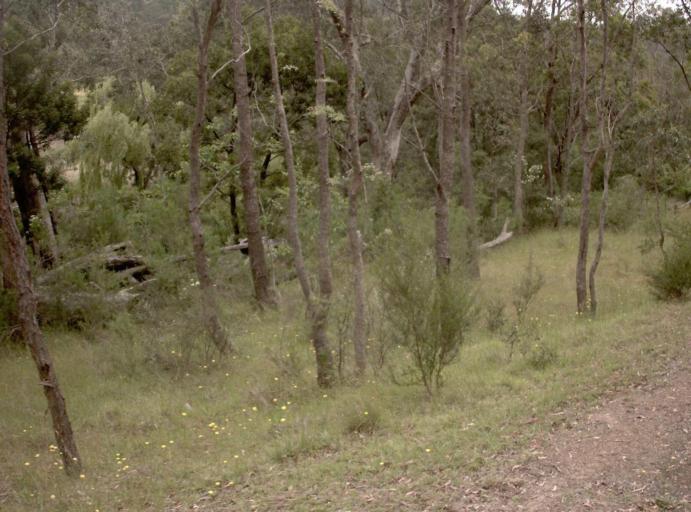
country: AU
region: Victoria
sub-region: East Gippsland
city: Bairnsdale
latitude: -37.5373
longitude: 147.2106
